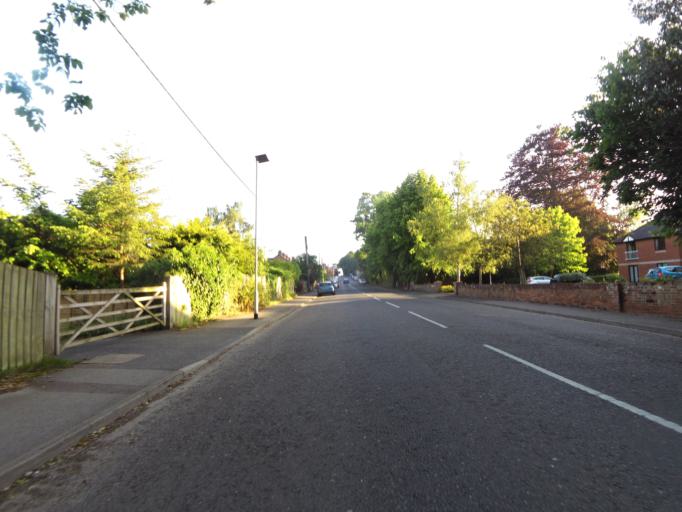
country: GB
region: England
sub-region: Suffolk
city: Woodbridge
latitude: 52.0992
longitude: 1.3247
